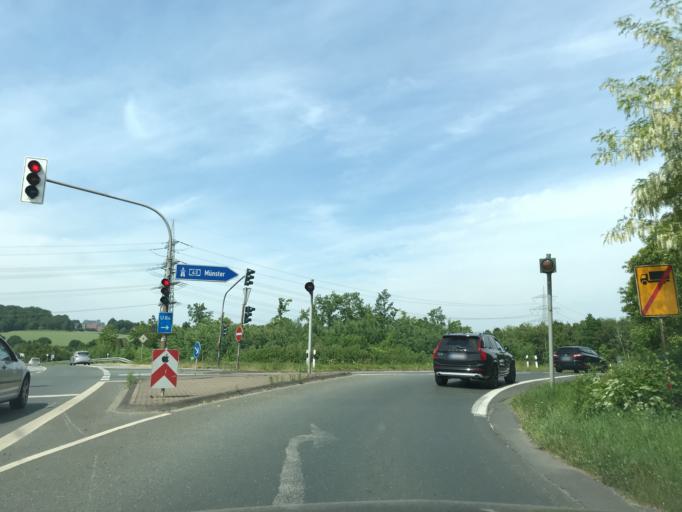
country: DE
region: North Rhine-Westphalia
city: Witten
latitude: 51.4340
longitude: 7.2901
